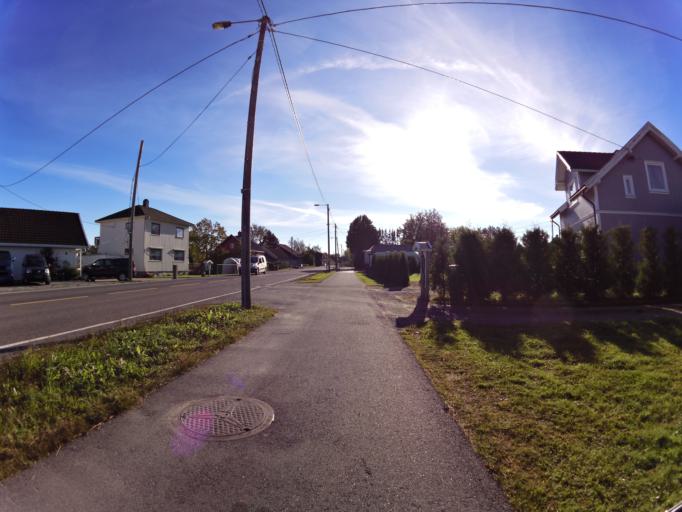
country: NO
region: Ostfold
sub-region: Sarpsborg
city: Sarpsborg
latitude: 59.2721
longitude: 11.0198
